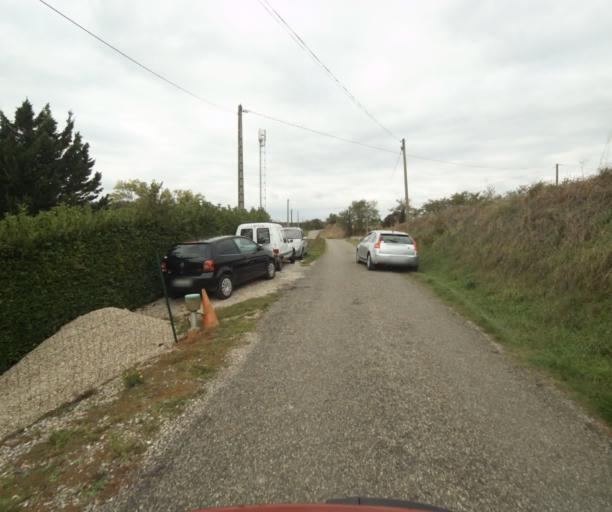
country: FR
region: Midi-Pyrenees
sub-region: Departement du Tarn-et-Garonne
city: Finhan
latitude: 43.8986
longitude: 1.2297
